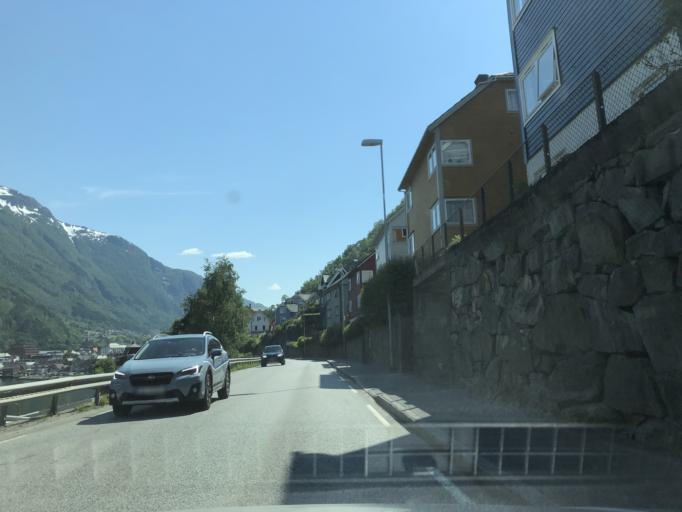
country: NO
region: Hordaland
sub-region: Odda
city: Odda
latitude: 60.0743
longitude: 6.5377
